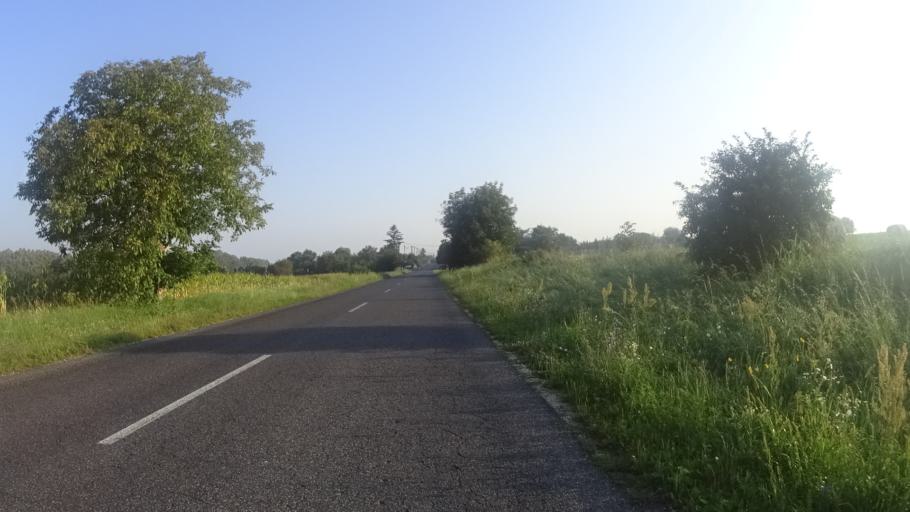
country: HU
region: Zala
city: Zalakomar
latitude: 46.5847
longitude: 17.1769
